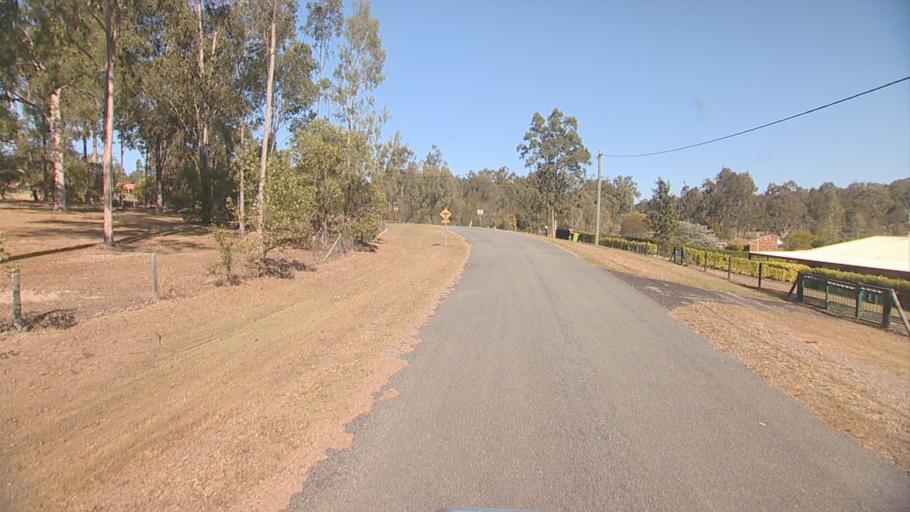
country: AU
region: Queensland
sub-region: Logan
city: Cedar Vale
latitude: -27.8572
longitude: 153.0346
